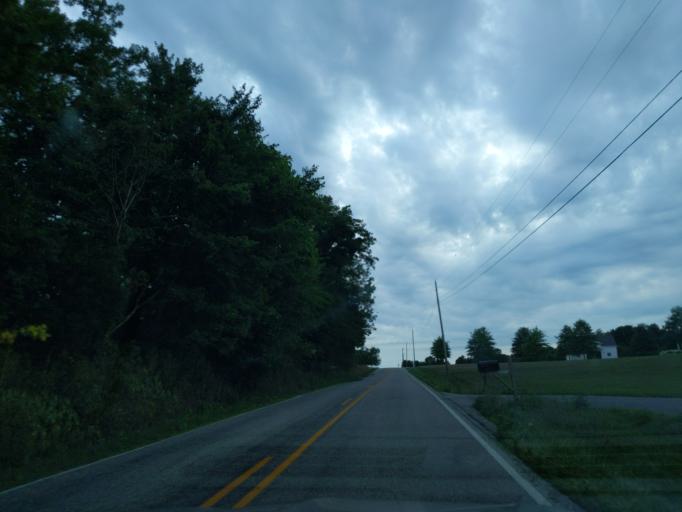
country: US
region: Indiana
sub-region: Ripley County
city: Sunman
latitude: 39.2034
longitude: -85.1663
